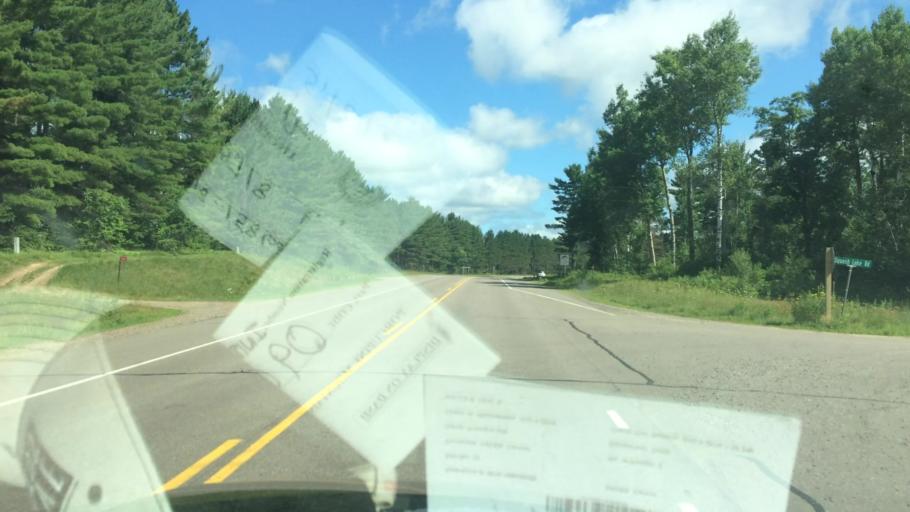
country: US
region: Wisconsin
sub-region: Oneida County
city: Rhinelander
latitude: 45.5883
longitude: -89.5694
